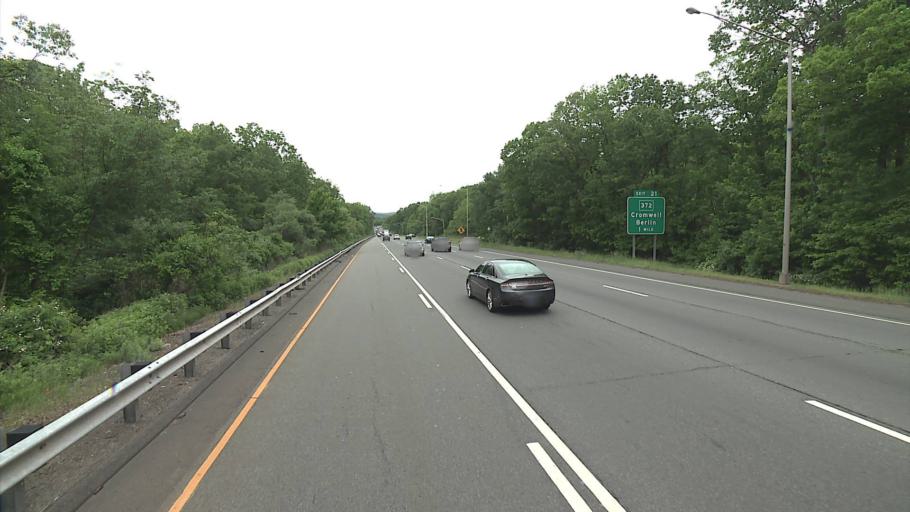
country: US
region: Connecticut
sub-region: Middlesex County
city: Cromwell
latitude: 41.6229
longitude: -72.6944
